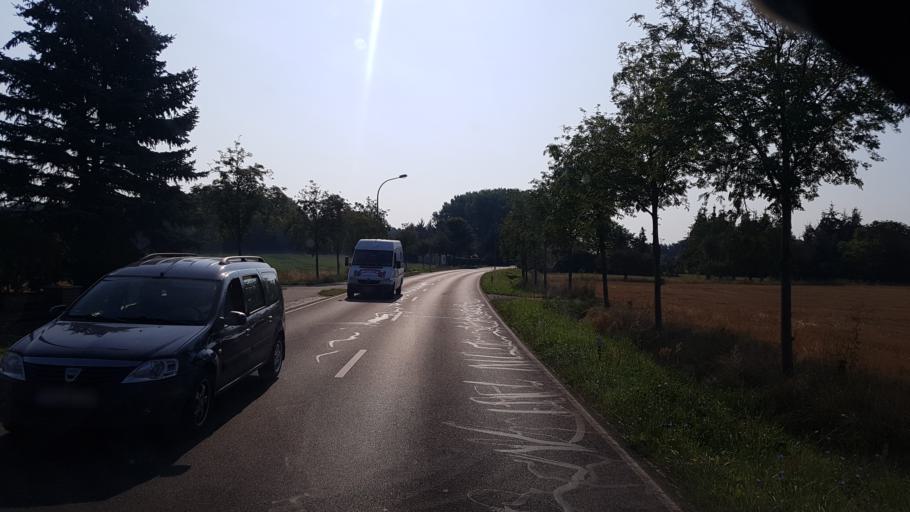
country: DE
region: Brandenburg
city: Drebkau
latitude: 51.6948
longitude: 14.2605
